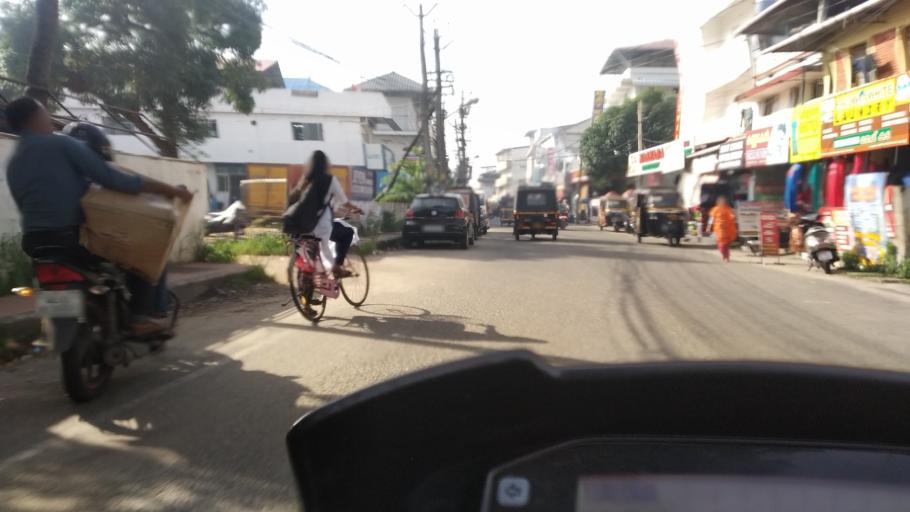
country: IN
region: Kerala
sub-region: Ernakulam
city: Elur
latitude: 10.0036
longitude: 76.2954
